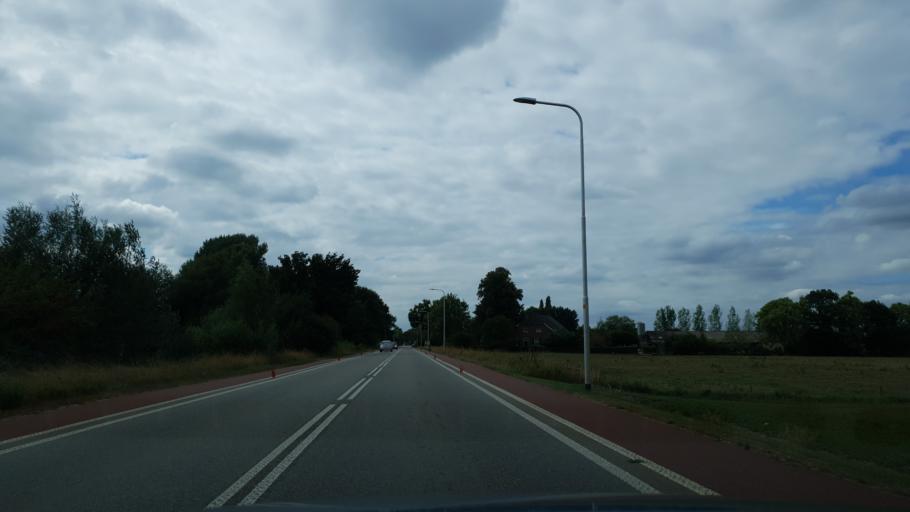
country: NL
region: North Brabant
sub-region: Gemeente Grave
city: Grave
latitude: 51.7717
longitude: 5.7560
